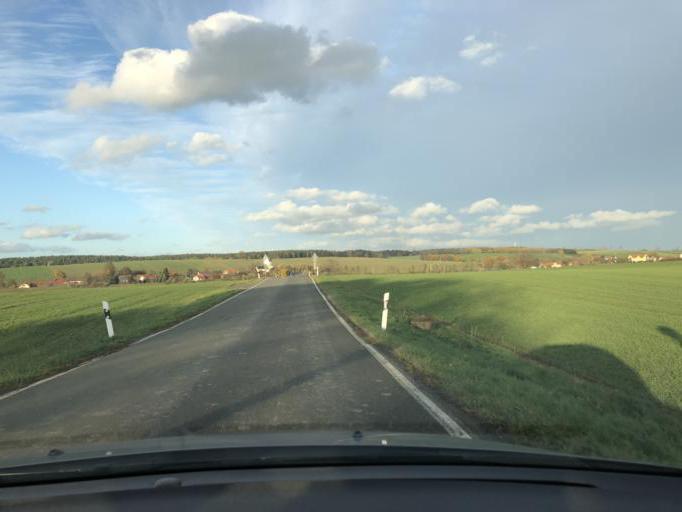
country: DE
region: Thuringia
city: Miesitz
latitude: 50.7355
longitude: 11.8207
